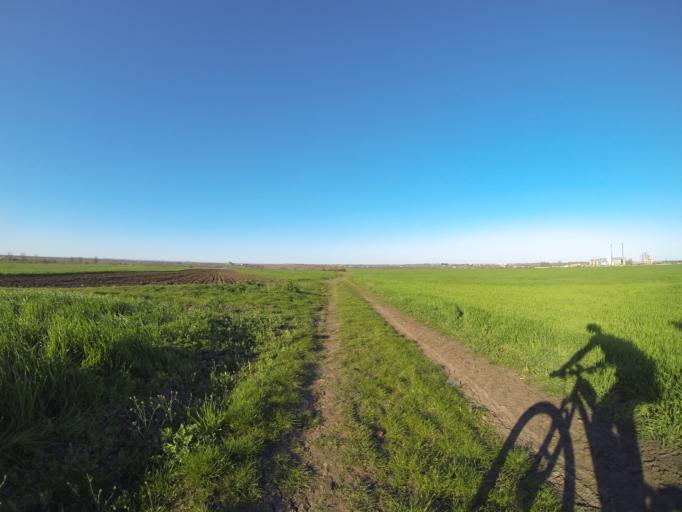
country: RO
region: Dolj
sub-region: Comuna Segarcea
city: Segarcea
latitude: 44.0843
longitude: 23.7104
